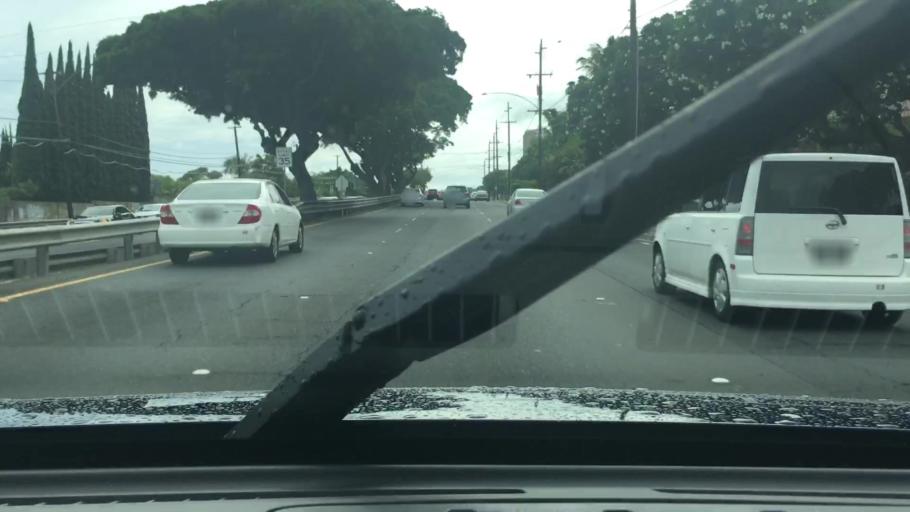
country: US
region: Hawaii
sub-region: Honolulu County
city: Honolulu
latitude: 21.2776
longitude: -157.7769
